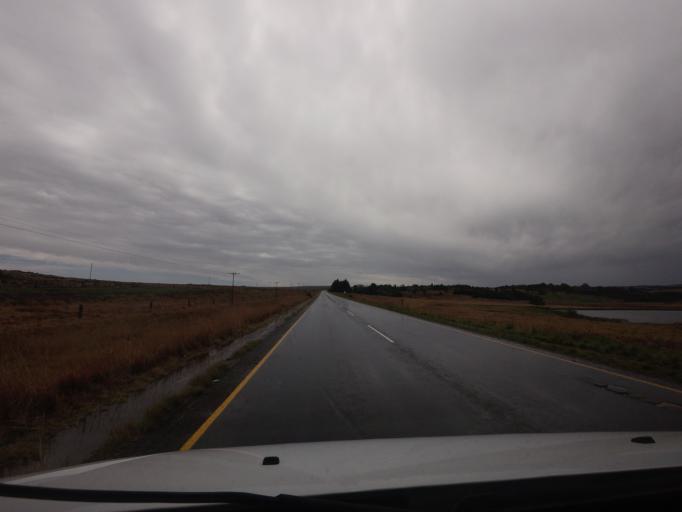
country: ZA
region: Mpumalanga
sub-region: Nkangala District Municipality
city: Belfast
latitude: -25.4457
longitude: 30.0964
